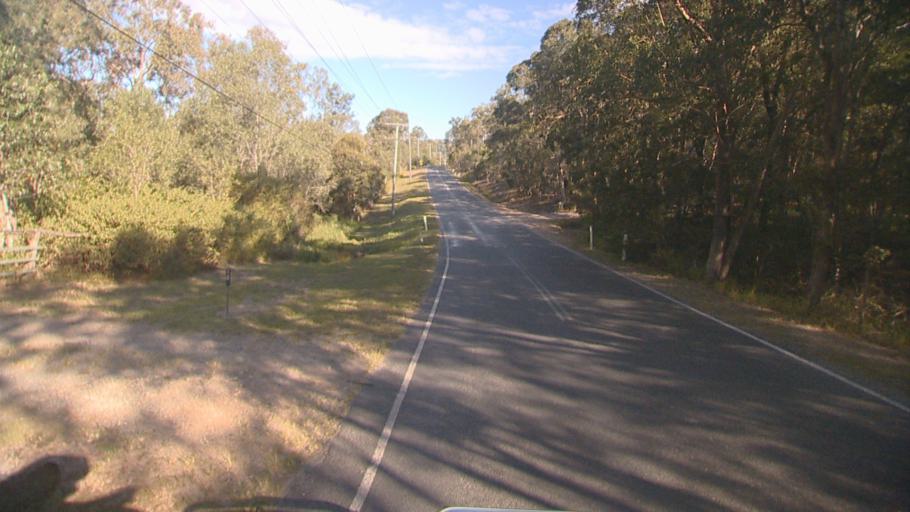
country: AU
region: Queensland
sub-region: Logan
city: Windaroo
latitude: -27.7287
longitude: 153.1717
